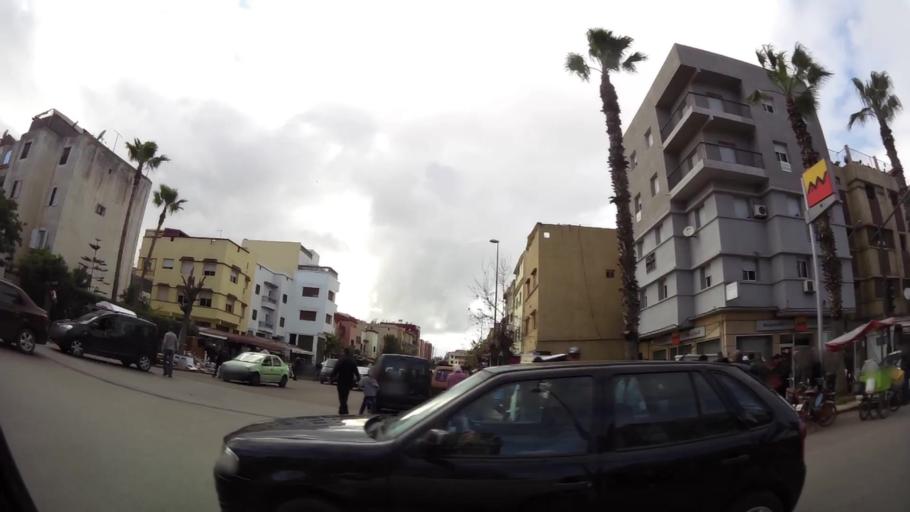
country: MA
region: Grand Casablanca
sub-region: Mohammedia
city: Mohammedia
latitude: 33.6790
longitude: -7.3917
